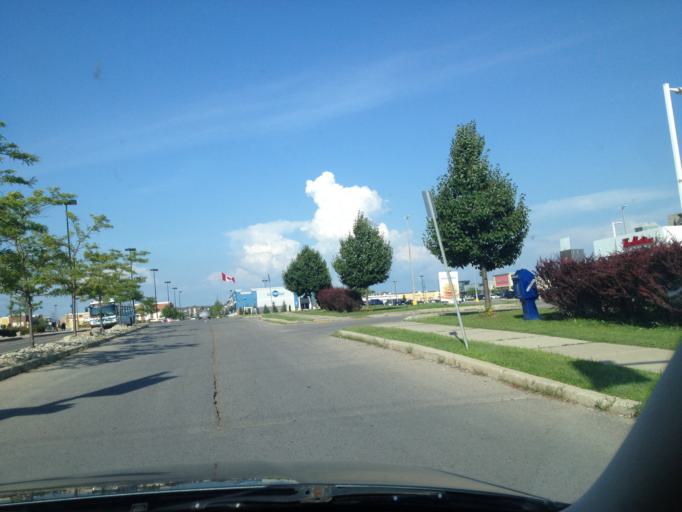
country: CA
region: Ontario
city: London
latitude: 43.0082
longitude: -81.3366
